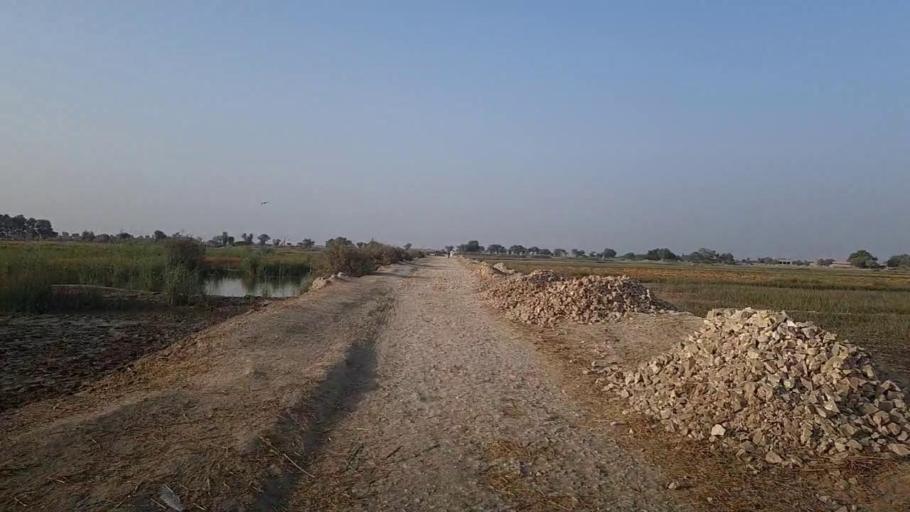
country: PK
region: Sindh
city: Tangwani
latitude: 28.2502
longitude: 69.0690
